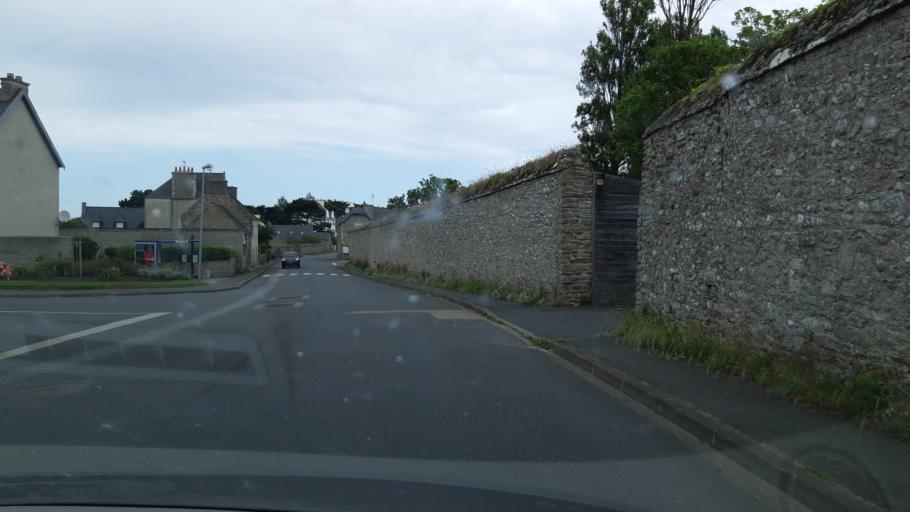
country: FR
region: Brittany
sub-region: Departement du Finistere
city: Roscoff
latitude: 48.7186
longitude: -3.9850
